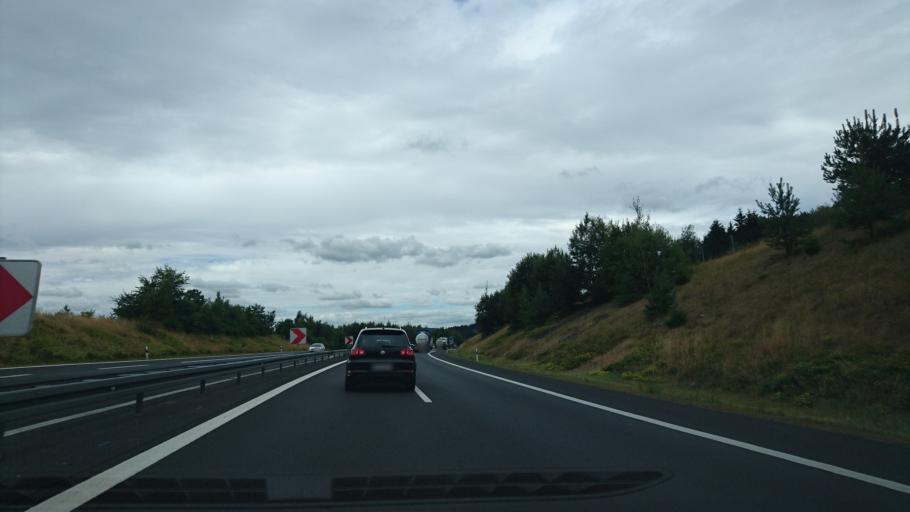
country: DE
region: Bavaria
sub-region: Upper Palatinate
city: Pechbrunn
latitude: 49.9779
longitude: 12.1396
